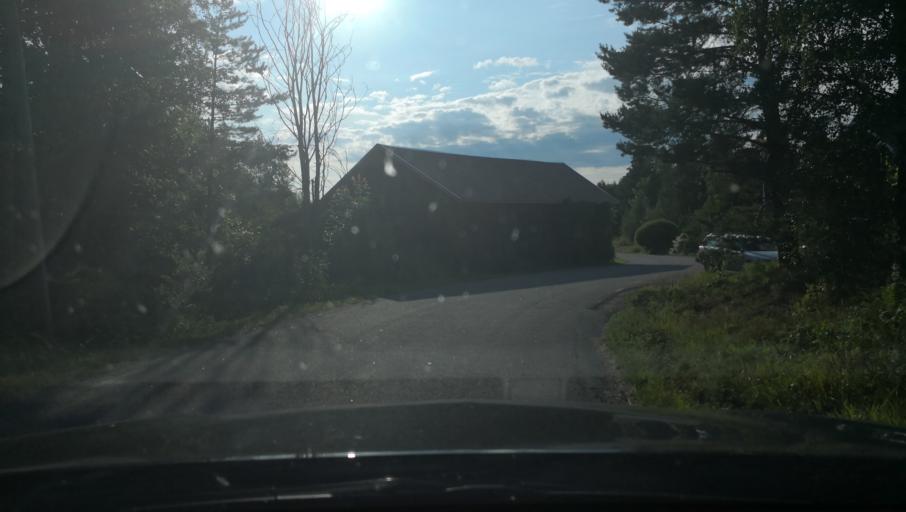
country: SE
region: Uppsala
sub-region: Osthammars Kommun
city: Osterbybruk
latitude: 60.0175
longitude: 17.9256
